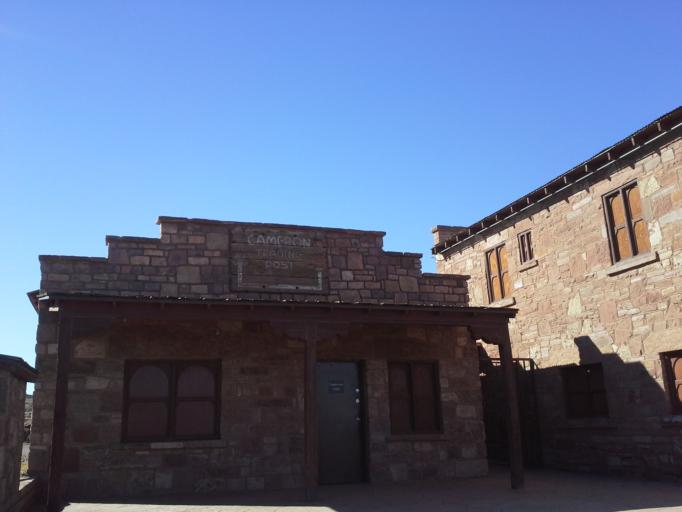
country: US
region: Arizona
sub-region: Coconino County
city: Tuba City
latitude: 35.8752
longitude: -111.4135
